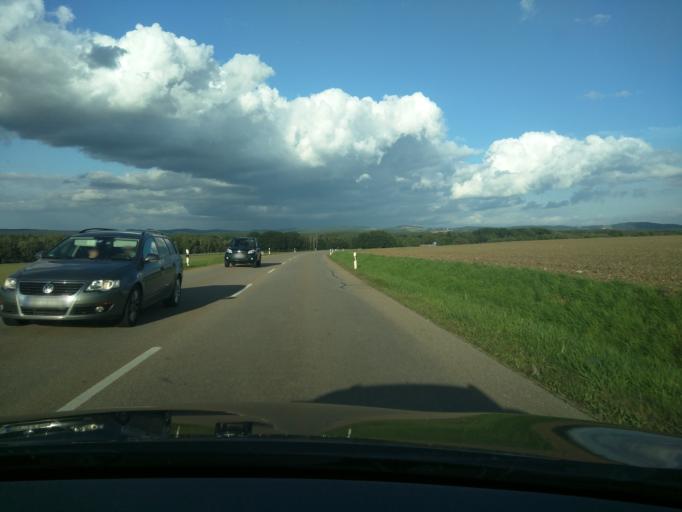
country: DE
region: Bavaria
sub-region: Upper Palatinate
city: Schwandorf in Bayern
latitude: 49.3451
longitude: 12.1321
